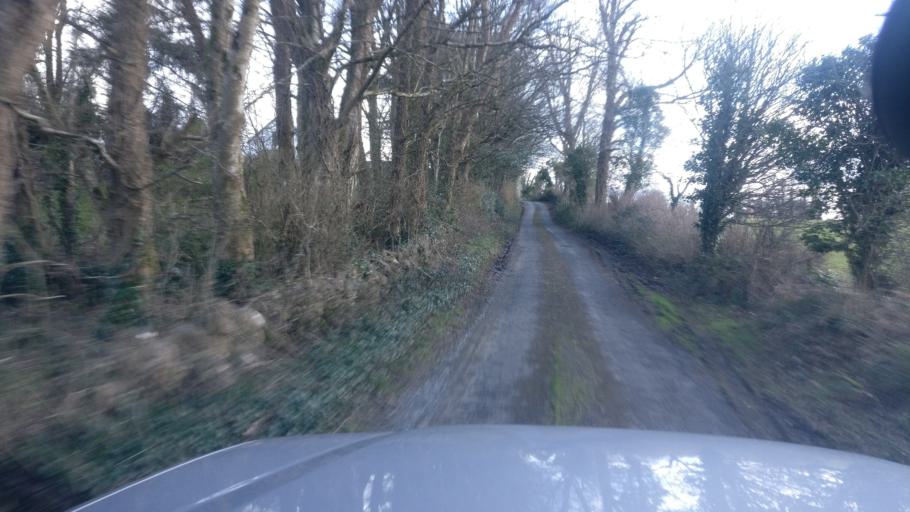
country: IE
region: Connaught
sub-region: County Galway
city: Loughrea
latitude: 53.1854
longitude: -8.4278
